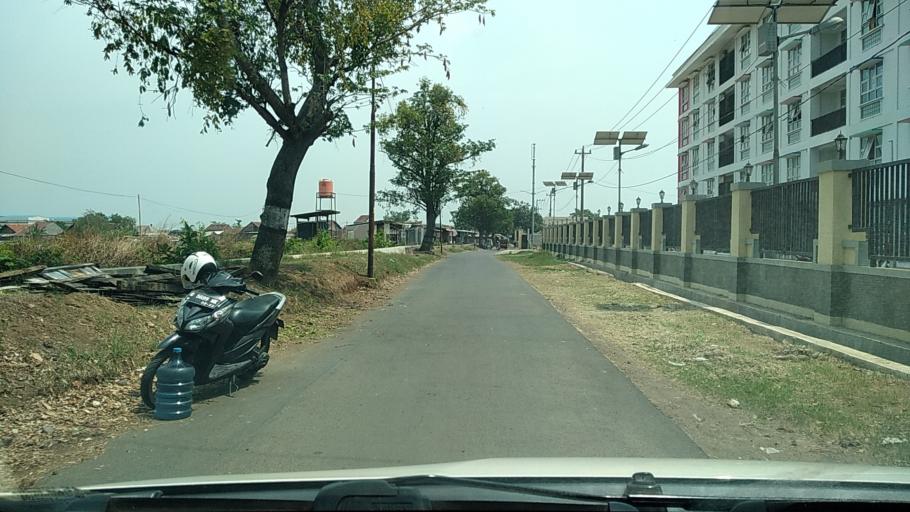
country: ID
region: Central Java
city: Semarang
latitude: -6.9827
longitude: 110.3637
